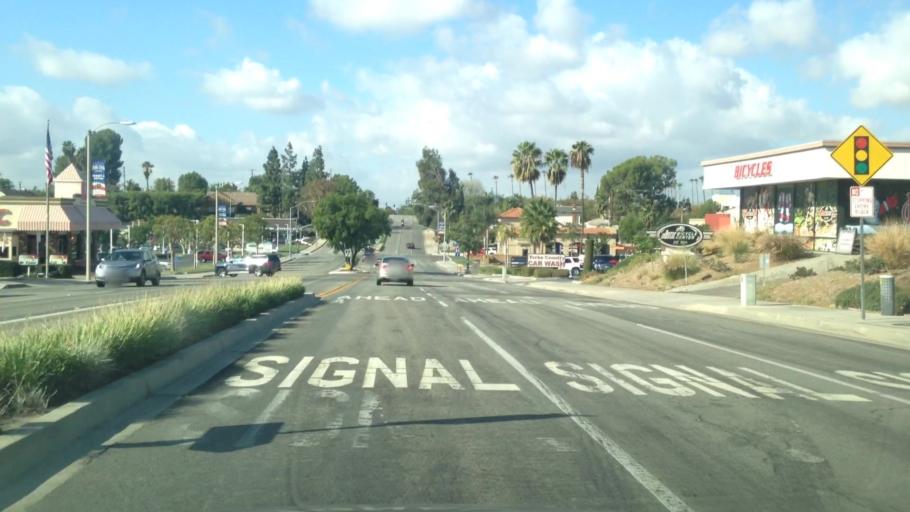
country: US
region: California
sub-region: Orange County
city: Yorba Linda
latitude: 33.8885
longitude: -117.8266
